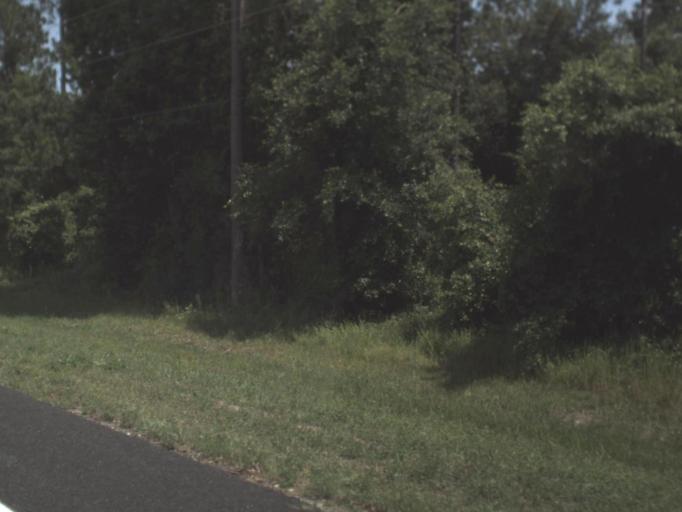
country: US
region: Florida
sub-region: Alachua County
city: Hawthorne
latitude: 29.6018
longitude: -82.2027
